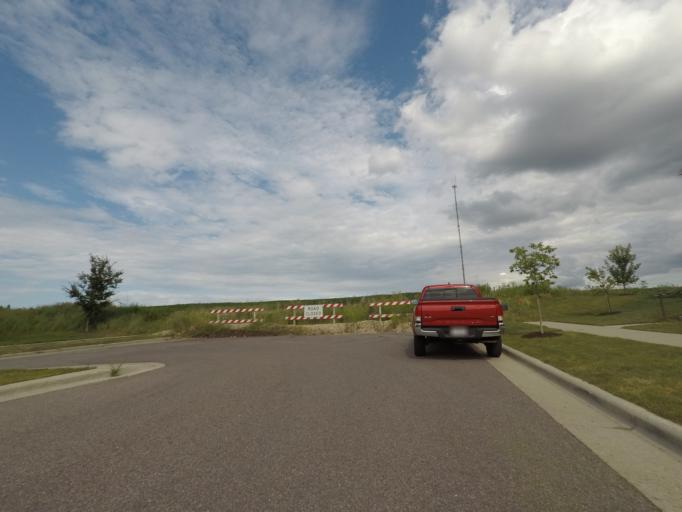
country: US
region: Wisconsin
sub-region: Dane County
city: Middleton
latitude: 43.0568
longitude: -89.5475
